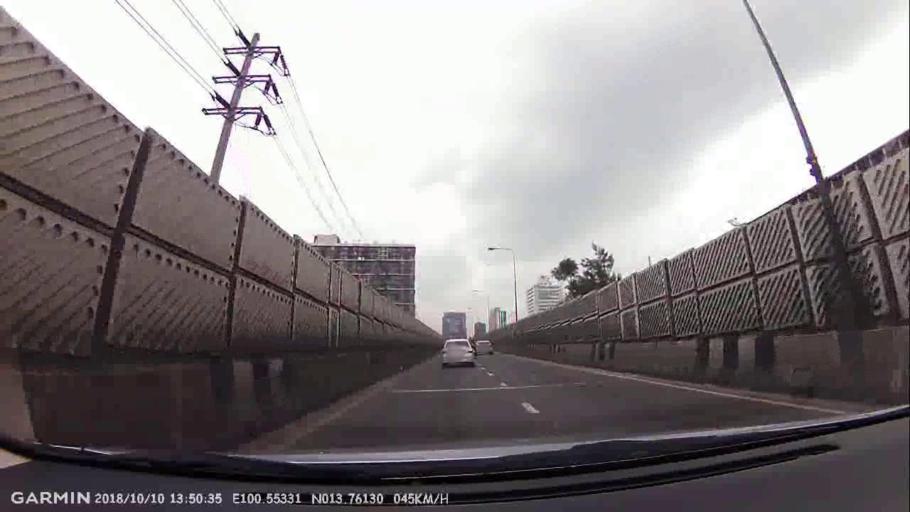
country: TH
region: Bangkok
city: Din Daeng
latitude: 13.7613
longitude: 100.5534
